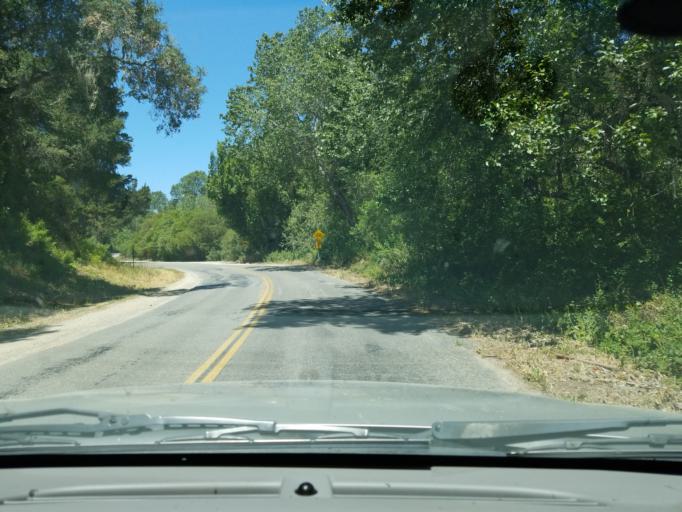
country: US
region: California
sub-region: Monterey County
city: Carmel Valley Village
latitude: 36.4460
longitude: -121.6809
